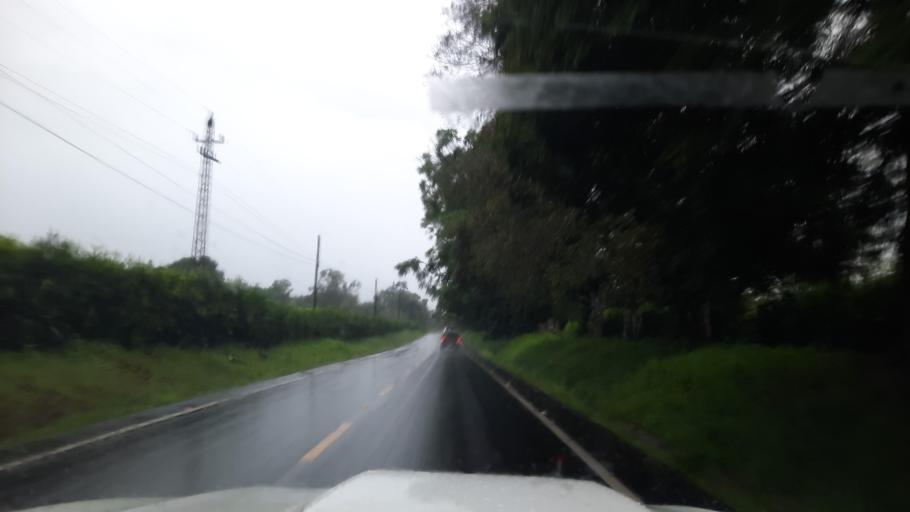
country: PA
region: Chiriqui
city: Sortova
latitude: 8.5682
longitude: -82.6318
